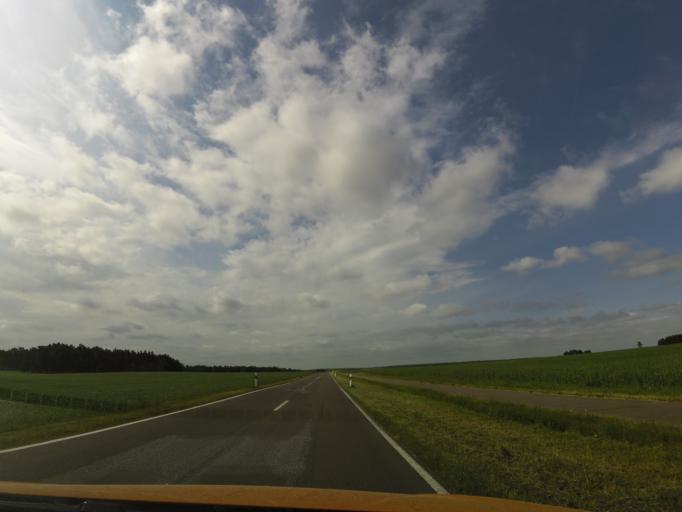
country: DE
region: Brandenburg
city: Belzig
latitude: 52.0838
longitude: 12.5341
